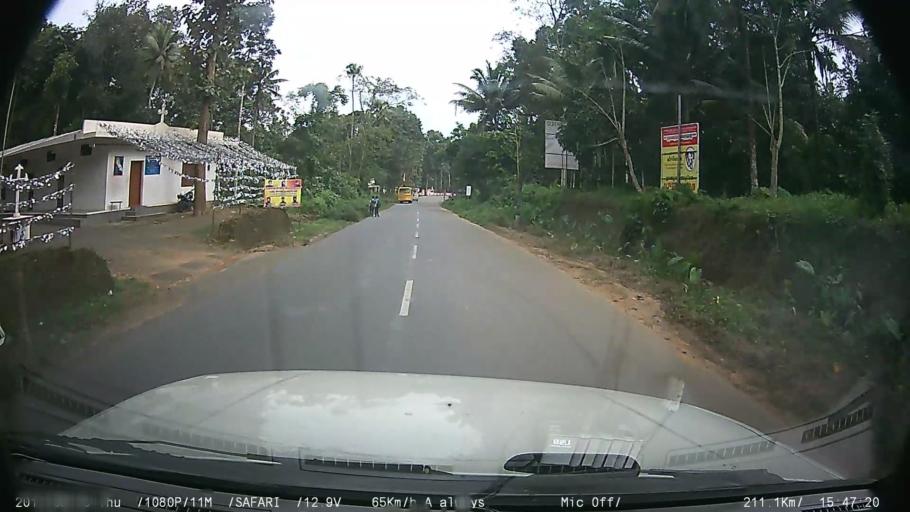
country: IN
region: Kerala
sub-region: Kottayam
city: Palackattumala
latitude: 9.8328
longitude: 76.5926
